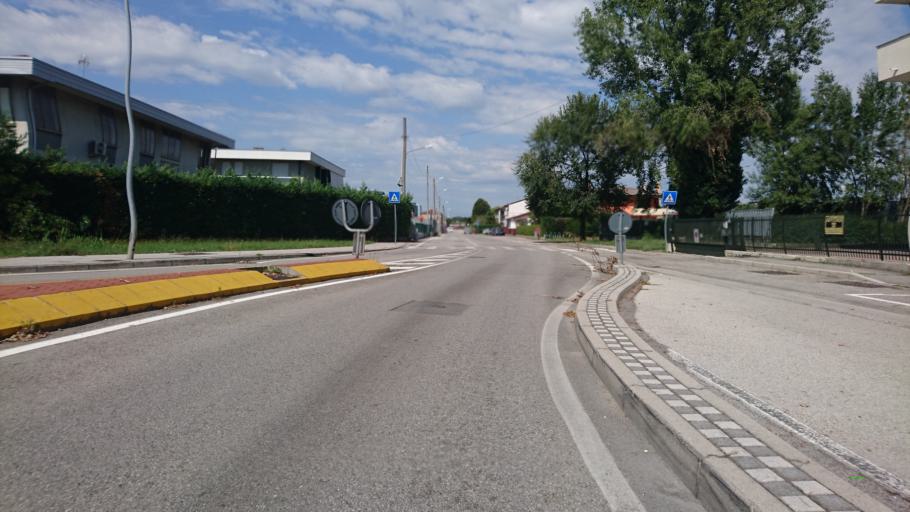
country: IT
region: Veneto
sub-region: Provincia di Padova
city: Noventa
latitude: 45.3996
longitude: 11.9367
